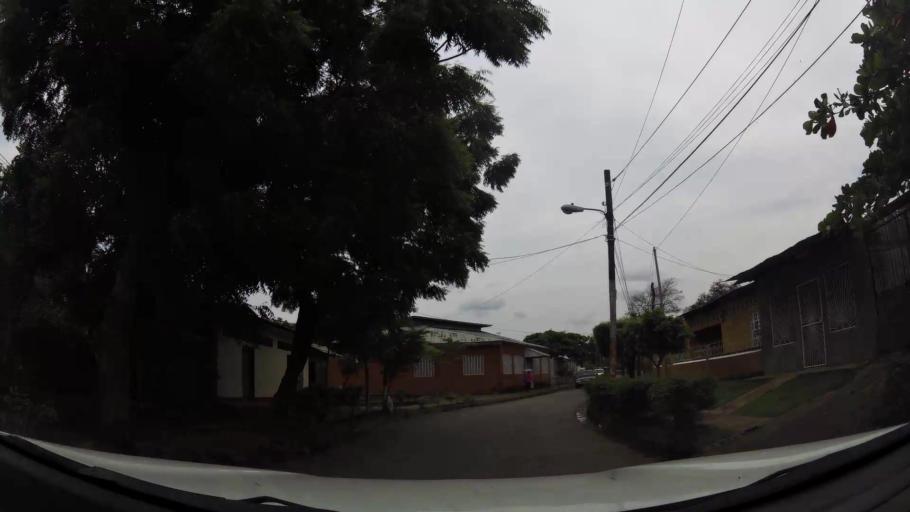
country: NI
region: Granada
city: Nandaime
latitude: 11.7563
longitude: -86.0471
